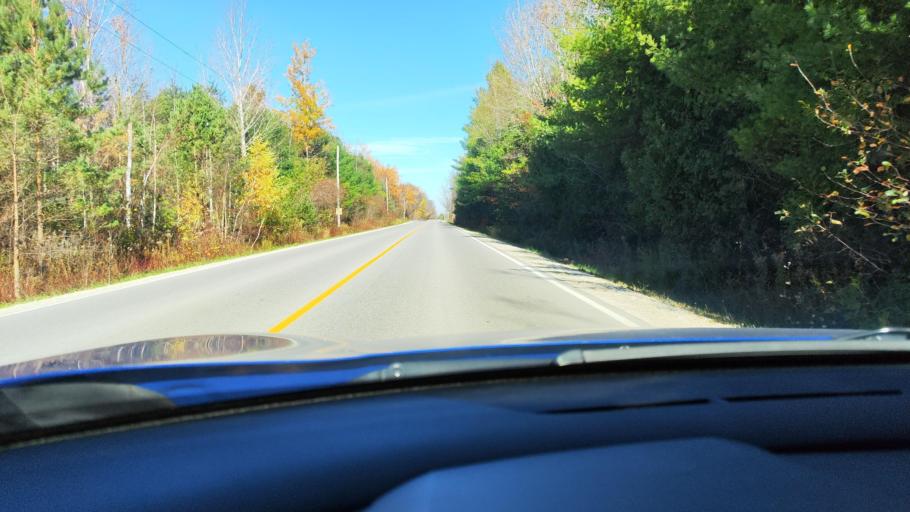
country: CA
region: Ontario
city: Wasaga Beach
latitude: 44.4070
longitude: -80.0593
